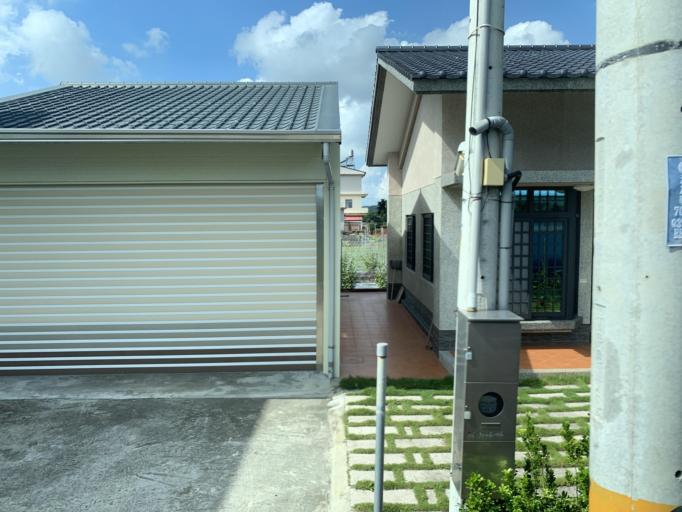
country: TW
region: Taiwan
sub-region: Pingtung
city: Pingtung
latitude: 22.8964
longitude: 120.5183
